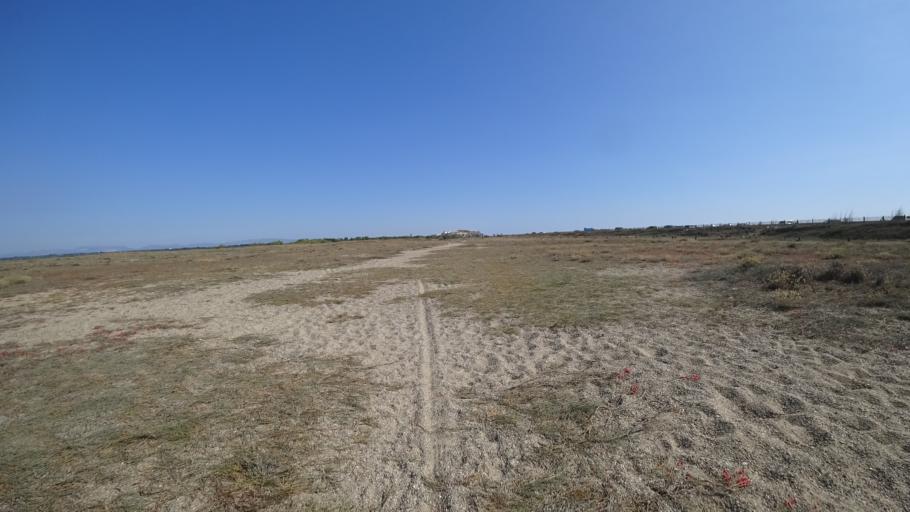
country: FR
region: Languedoc-Roussillon
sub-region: Departement des Pyrenees-Orientales
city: Saint-Cyprien-Plage
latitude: 42.6669
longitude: 3.0324
